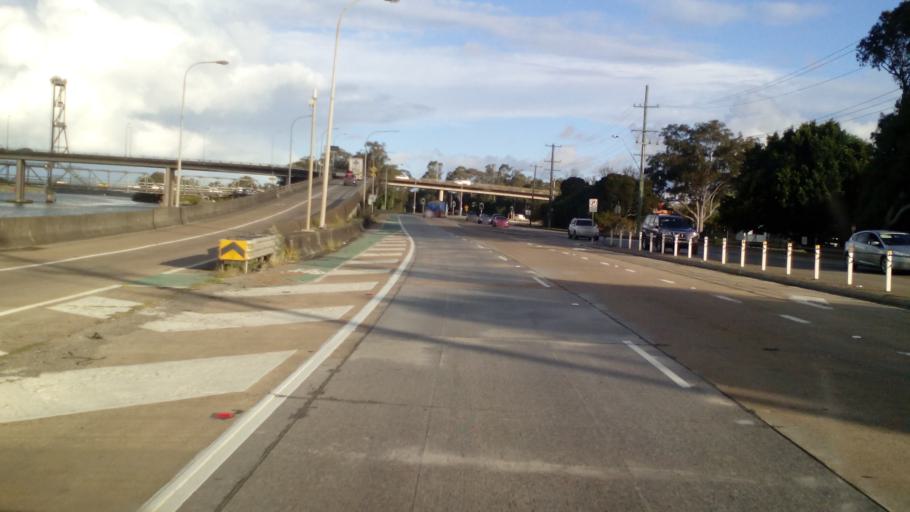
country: AU
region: New South Wales
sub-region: Newcastle
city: Beresfield
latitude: -32.8219
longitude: 151.6826
